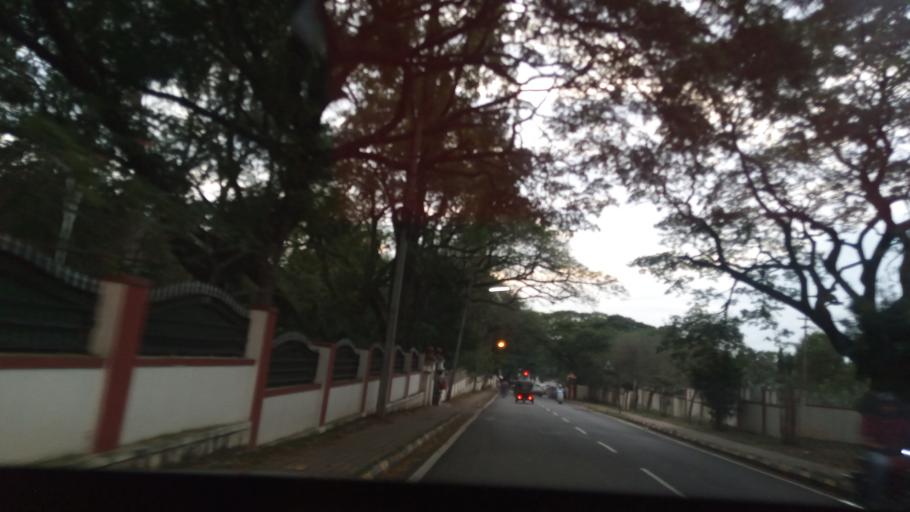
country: IN
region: Karnataka
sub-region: Mysore
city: Mysore
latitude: 12.3267
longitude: 76.6351
